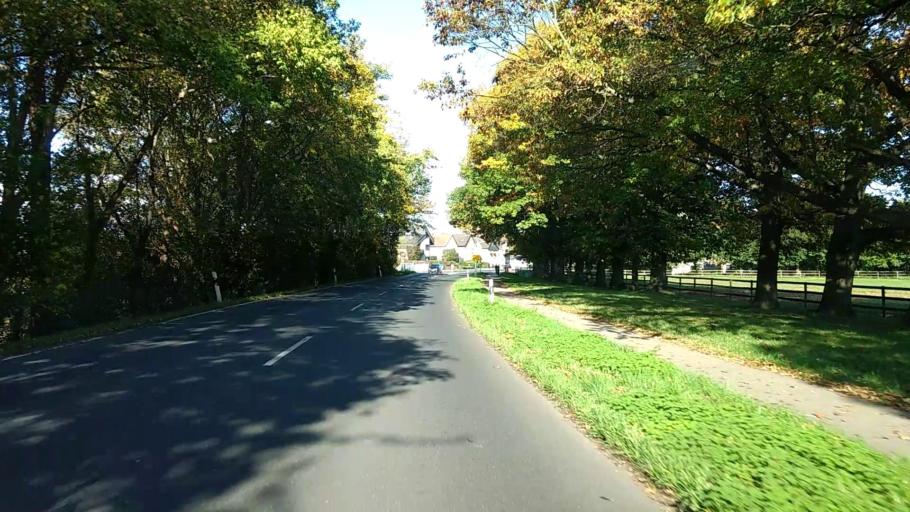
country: DE
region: North Rhine-Westphalia
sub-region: Regierungsbezirk Koln
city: Bergheim
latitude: 50.9281
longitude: 6.6842
